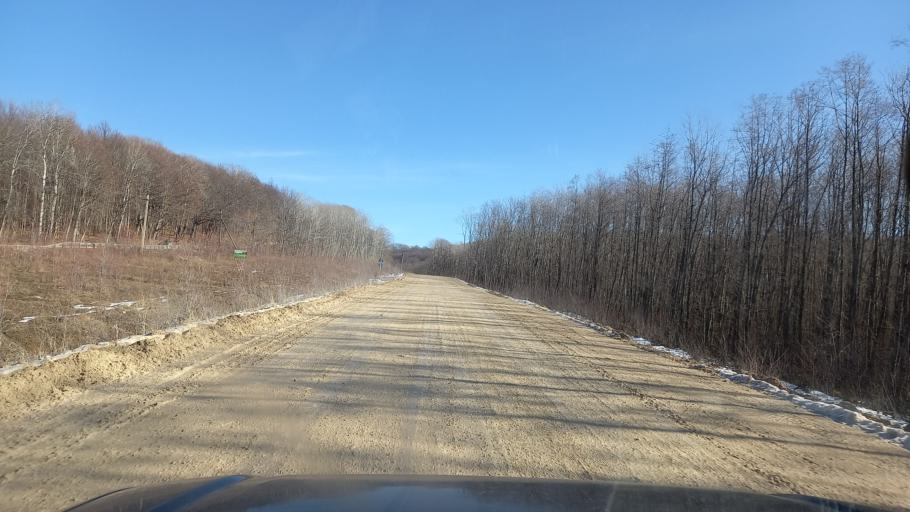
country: RU
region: Adygeya
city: Kamennomostskiy
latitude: 44.2867
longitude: 40.3017
